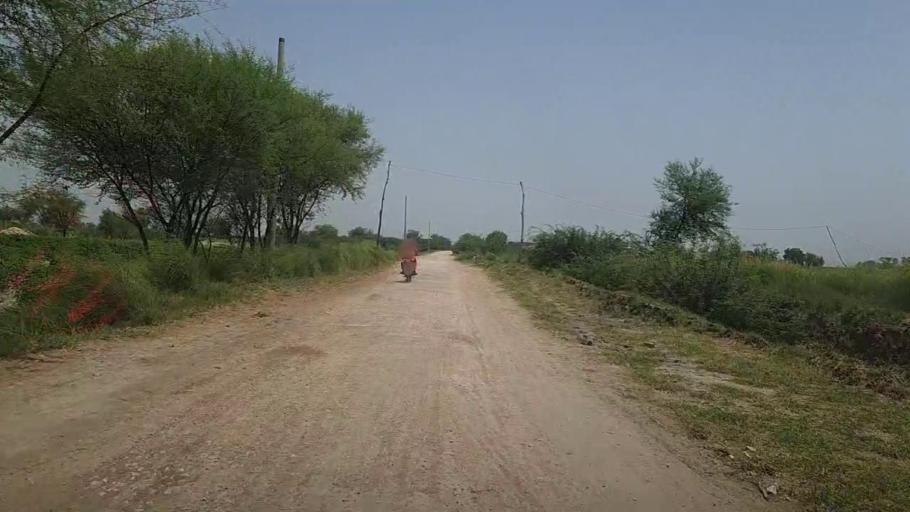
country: PK
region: Sindh
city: Pad Idan
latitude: 26.8446
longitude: 68.2804
